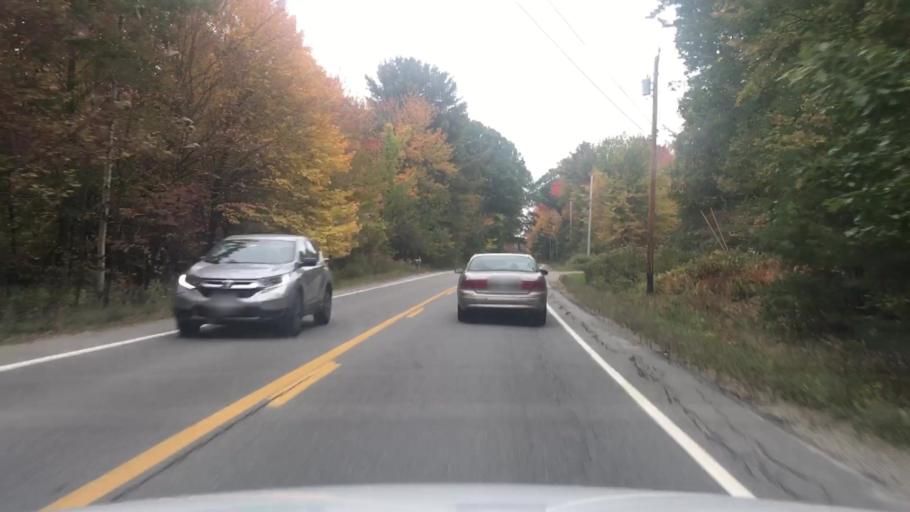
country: US
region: Maine
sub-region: Kennebec County
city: Oakland
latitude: 44.5400
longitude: -69.7927
